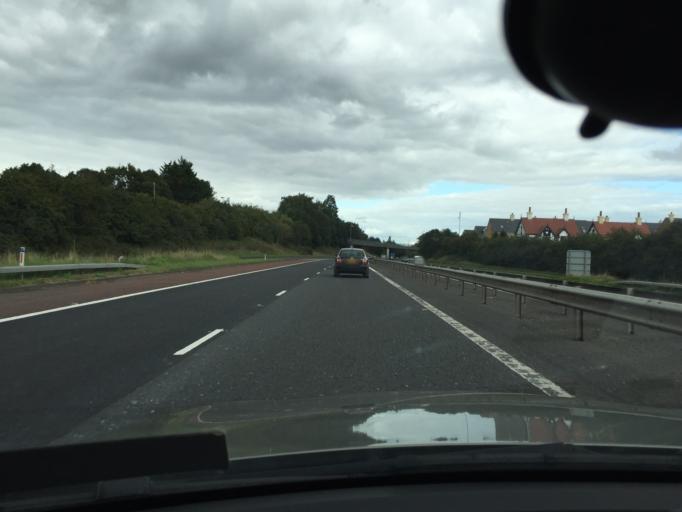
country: GB
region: Northern Ireland
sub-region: Lisburn District
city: Lisburn
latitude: 54.5067
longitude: -6.0275
